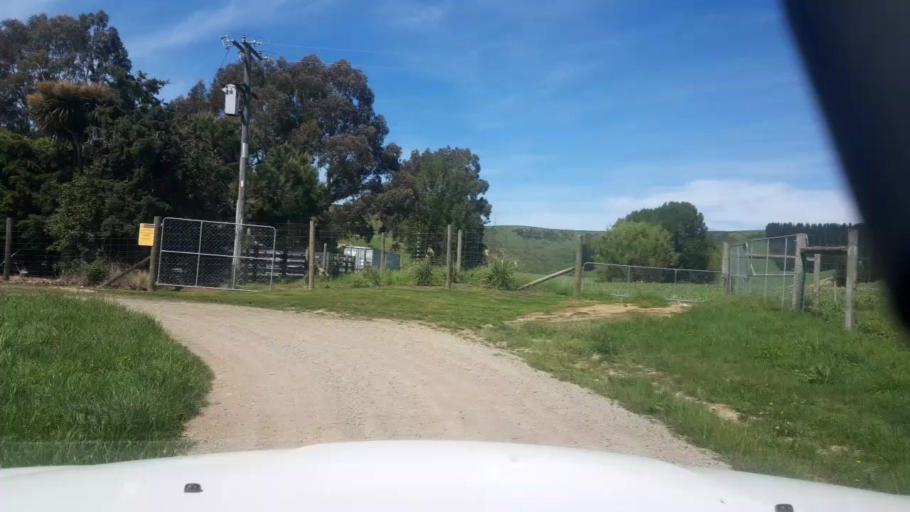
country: NZ
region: Canterbury
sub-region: Timaru District
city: Pleasant Point
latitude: -44.3198
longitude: 171.0995
